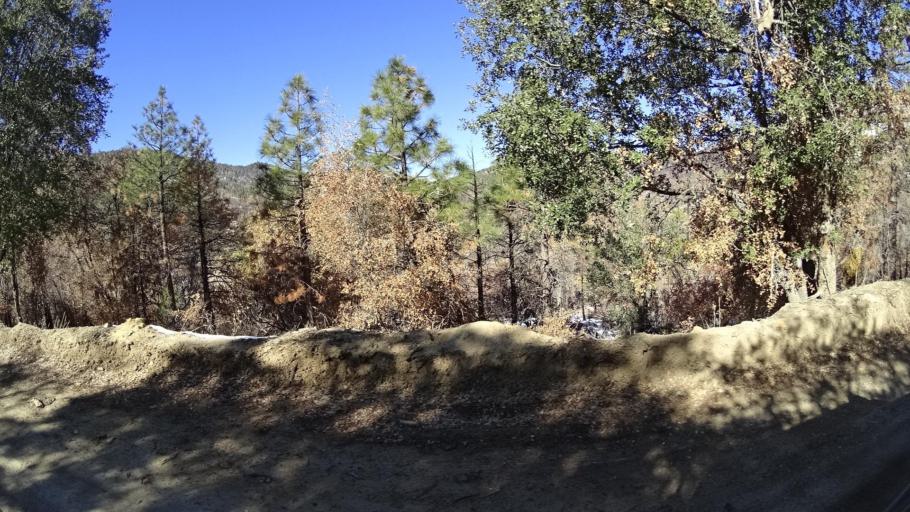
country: US
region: California
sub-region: Kern County
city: Alta Sierra
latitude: 35.7168
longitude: -118.5331
